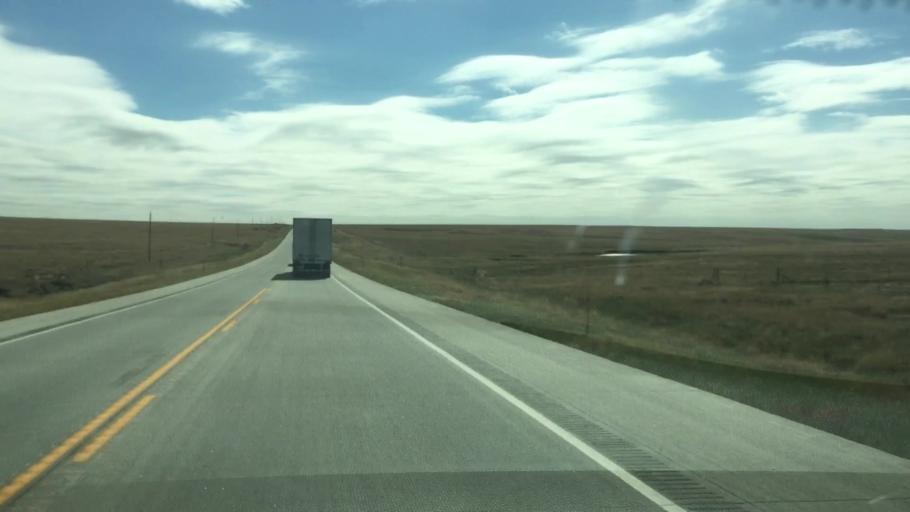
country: US
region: Colorado
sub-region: Lincoln County
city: Hugo
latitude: 39.0156
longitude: -103.3051
